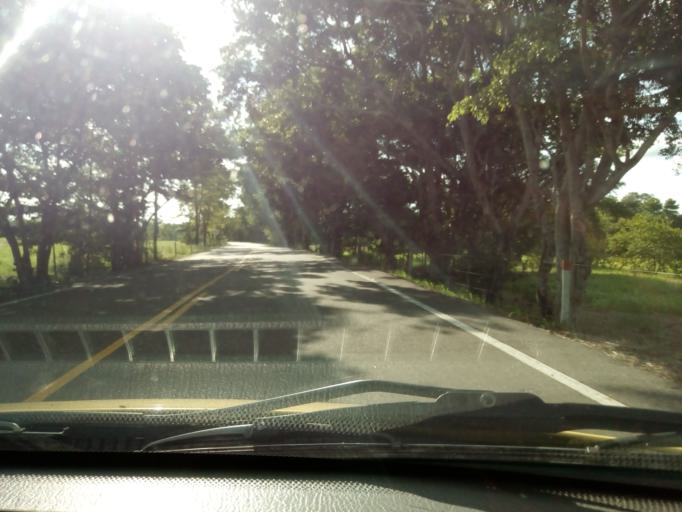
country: CO
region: Boyaca
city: Puerto Boyaca
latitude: 5.9364
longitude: -74.5147
